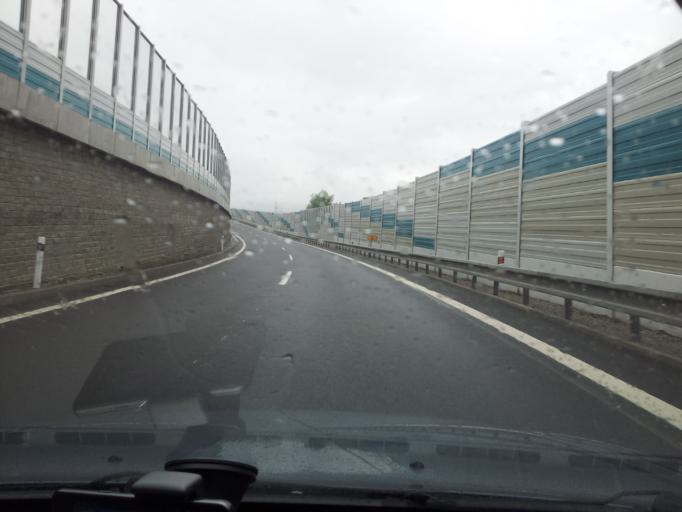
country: SK
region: Banskobystricky
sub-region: Okres Banska Bystrica
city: Banska Bystrica
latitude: 48.7432
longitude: 19.1591
